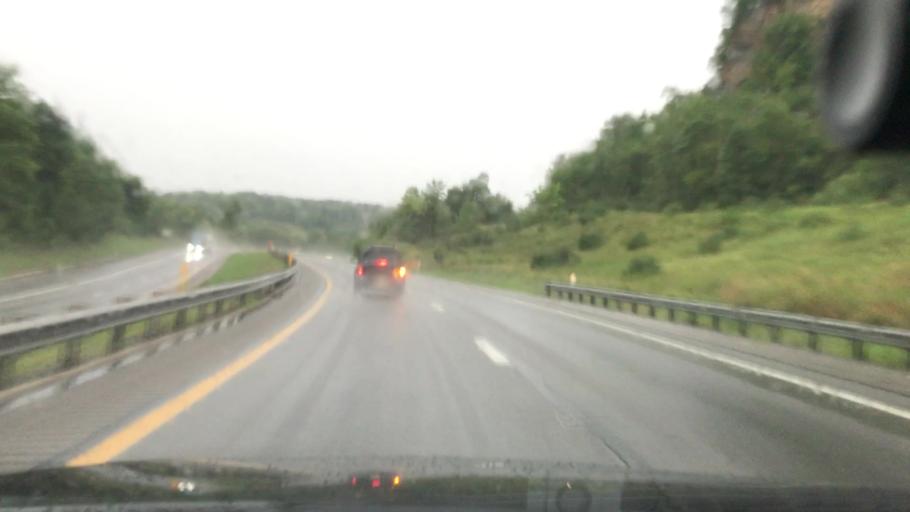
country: US
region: West Virginia
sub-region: Mercer County
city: Athens
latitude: 37.4625
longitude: -81.0666
